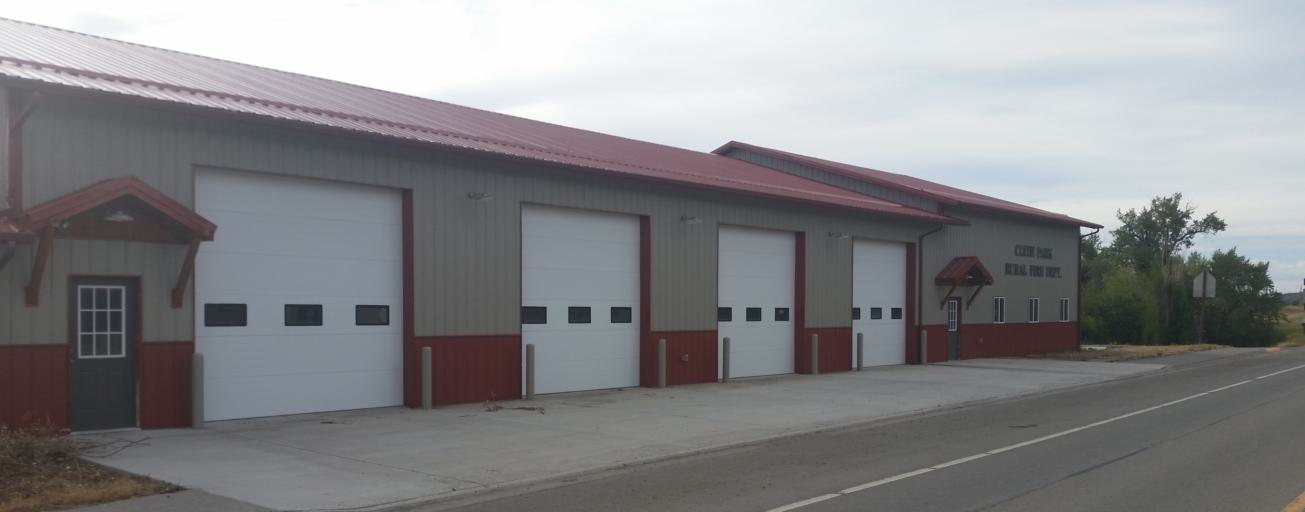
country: US
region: Montana
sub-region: Park County
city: Livingston
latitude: 45.8857
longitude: -110.6040
